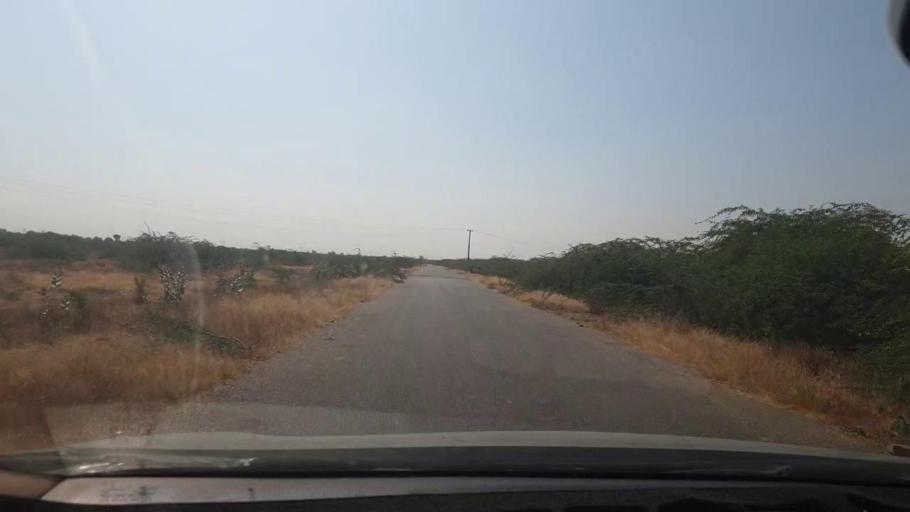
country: PK
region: Sindh
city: Malir Cantonment
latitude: 25.1613
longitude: 67.1513
